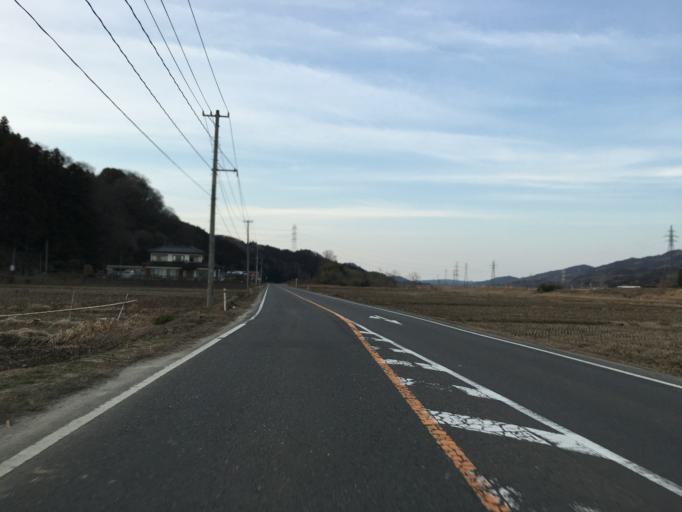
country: JP
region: Ibaraki
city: Daigo
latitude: 36.8808
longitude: 140.4142
